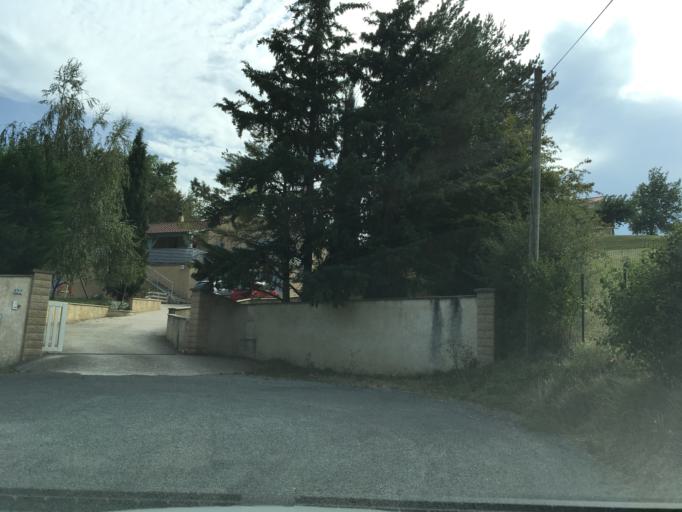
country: FR
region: Midi-Pyrenees
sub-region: Departement du Tarn
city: Lagarrigue
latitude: 43.6050
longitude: 2.2800
